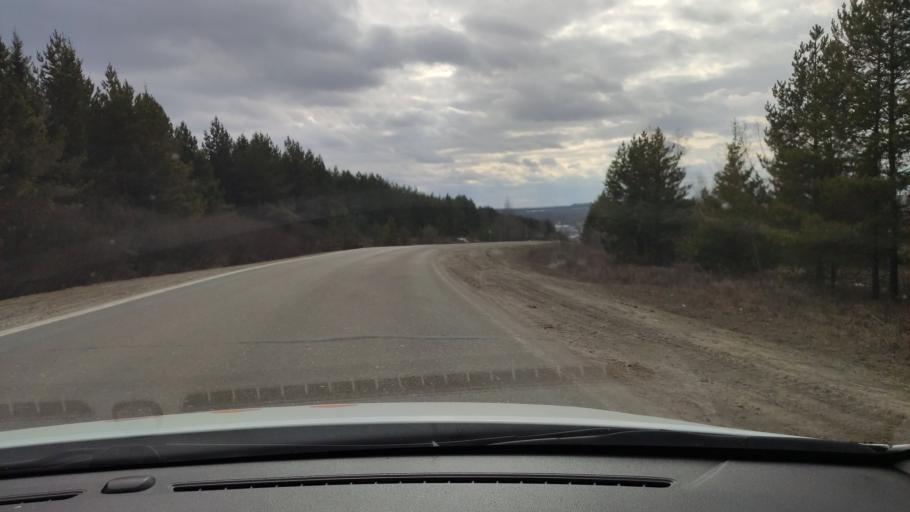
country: RU
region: Tatarstan
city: Vysokaya Gora
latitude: 56.1285
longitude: 49.2078
